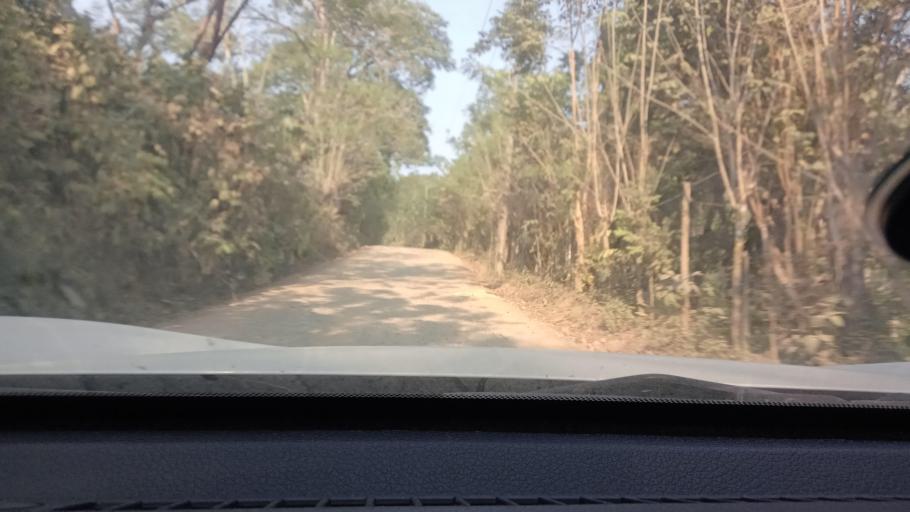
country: MX
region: Tabasco
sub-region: Huimanguillo
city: Francisco Rueda
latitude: 17.6557
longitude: -93.8733
